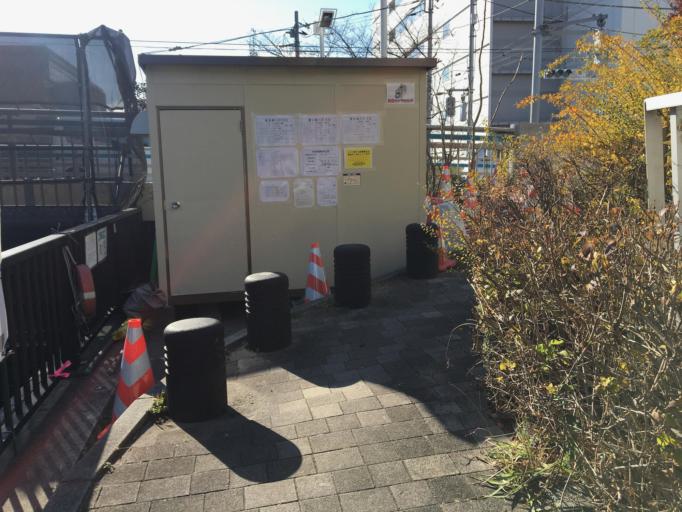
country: JP
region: Tokyo
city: Urayasu
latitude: 35.6793
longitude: 139.7938
